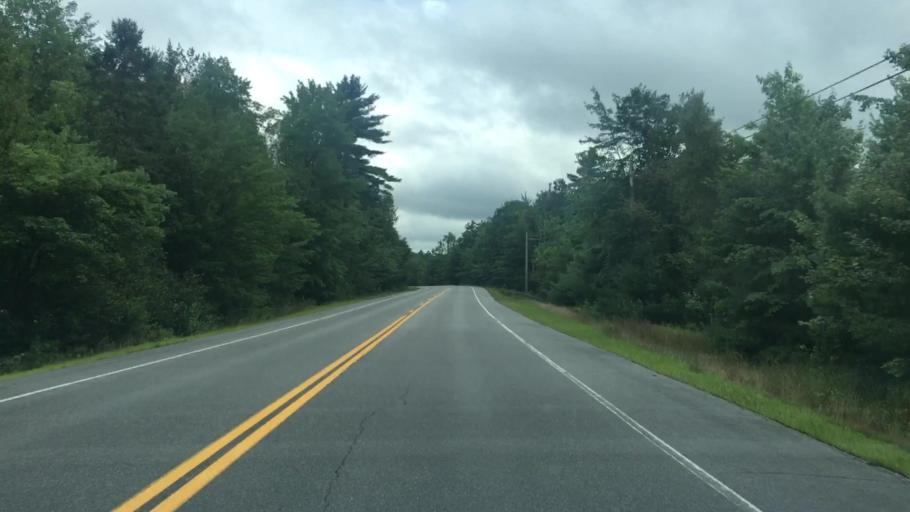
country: US
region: Maine
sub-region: York County
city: Cornish
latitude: 43.7735
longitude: -70.8207
